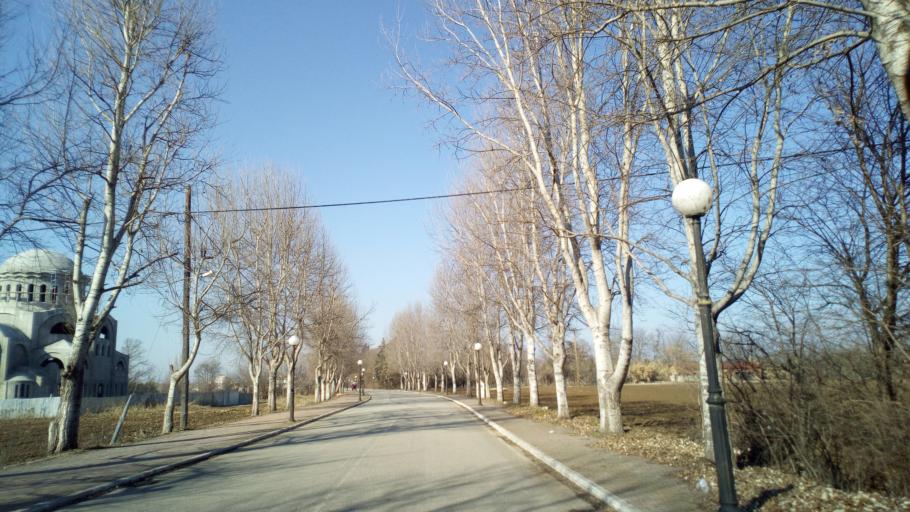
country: GR
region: Central Macedonia
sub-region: Nomos Thessalonikis
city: Lagkadas
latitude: 40.7382
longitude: 23.0818
